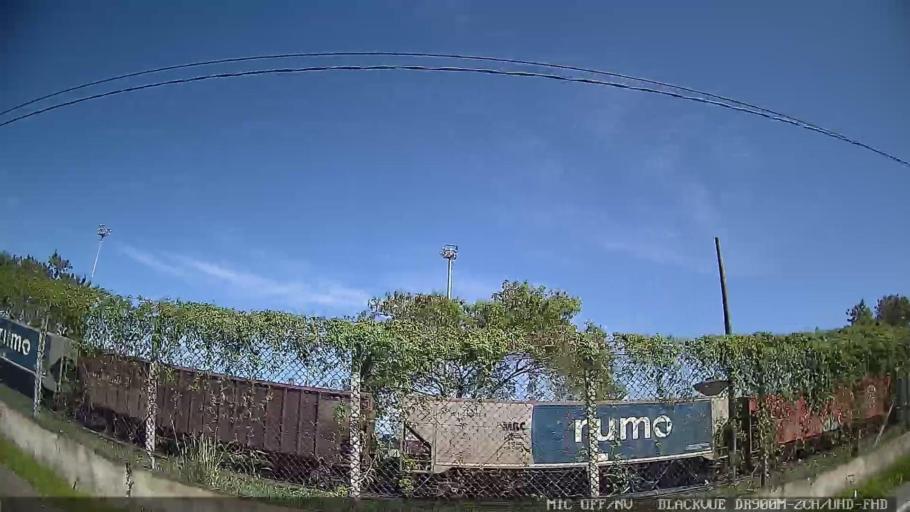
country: BR
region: Sao Paulo
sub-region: Santos
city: Santos
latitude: -23.9580
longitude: -46.2887
